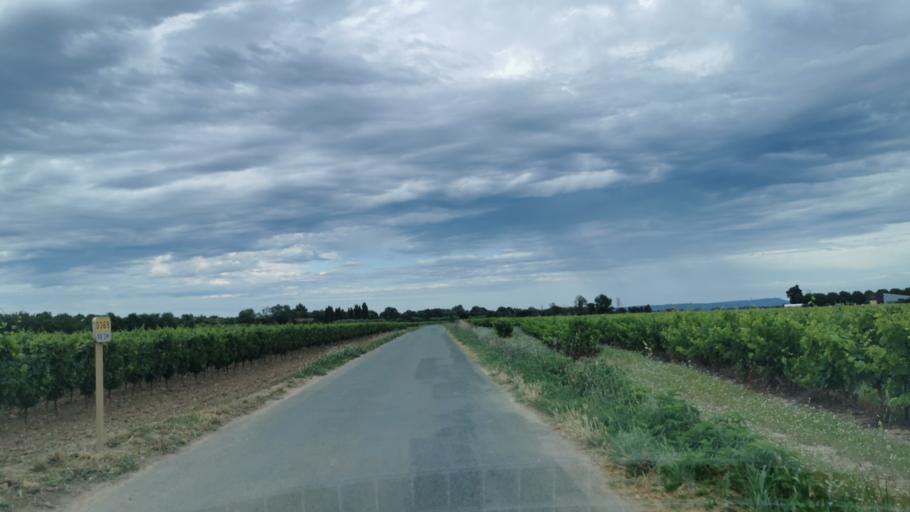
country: FR
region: Languedoc-Roussillon
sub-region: Departement de l'Aude
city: Moussan
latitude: 43.2452
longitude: 2.9770
